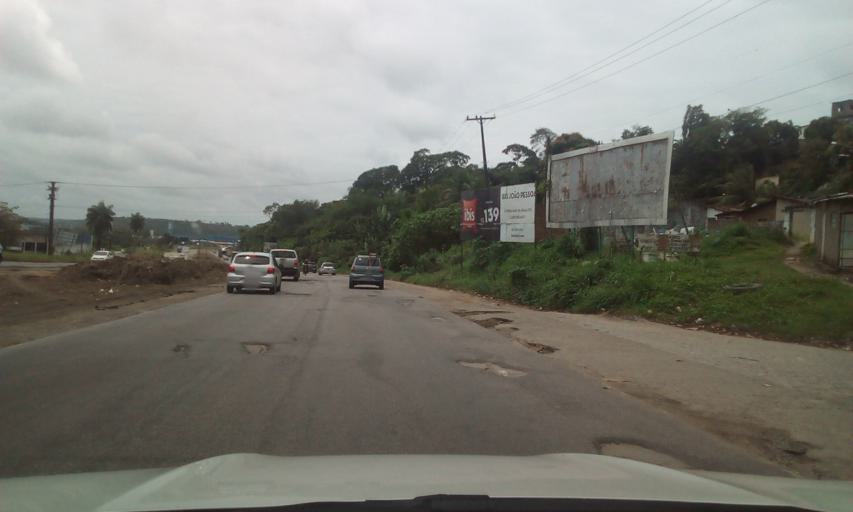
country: BR
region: Pernambuco
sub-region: Abreu E Lima
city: Abreu e Lima
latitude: -7.9284
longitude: -34.8982
